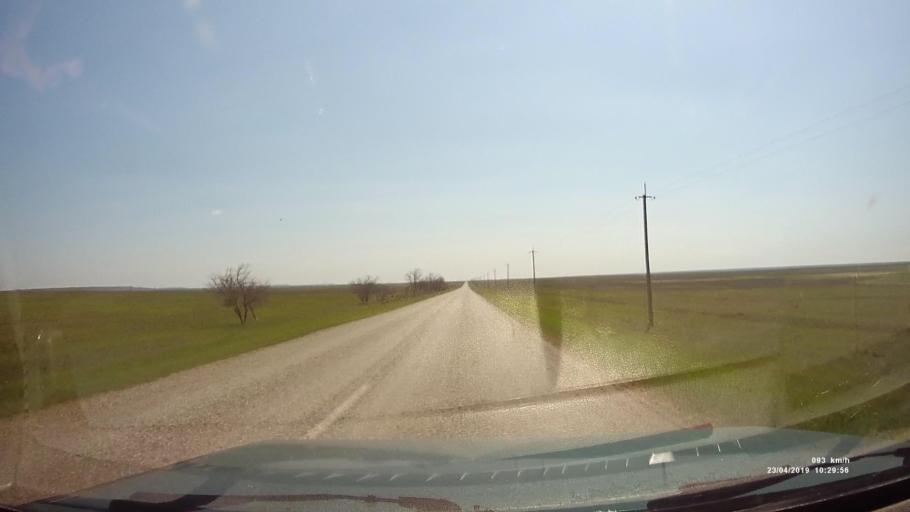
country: RU
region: Kalmykiya
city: Yashalta
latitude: 46.5955
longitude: 42.5349
